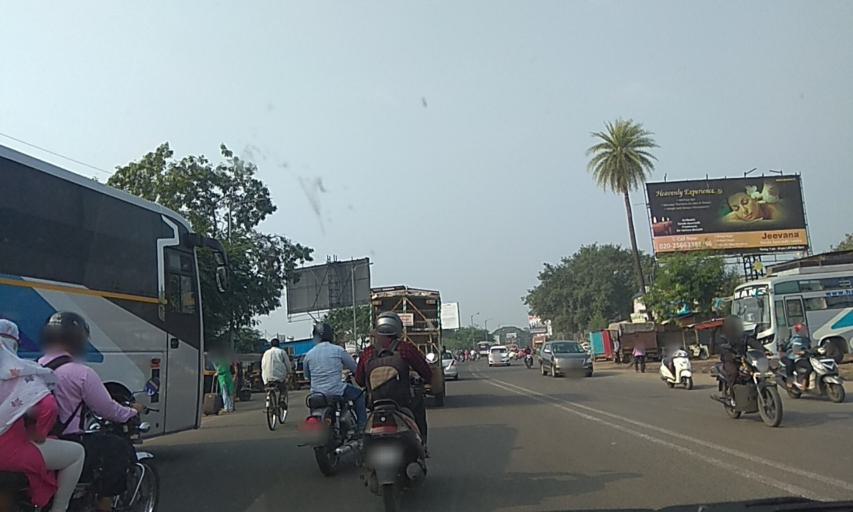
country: IN
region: Maharashtra
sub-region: Pune Division
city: Shivaji Nagar
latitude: 18.5385
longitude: 73.8647
